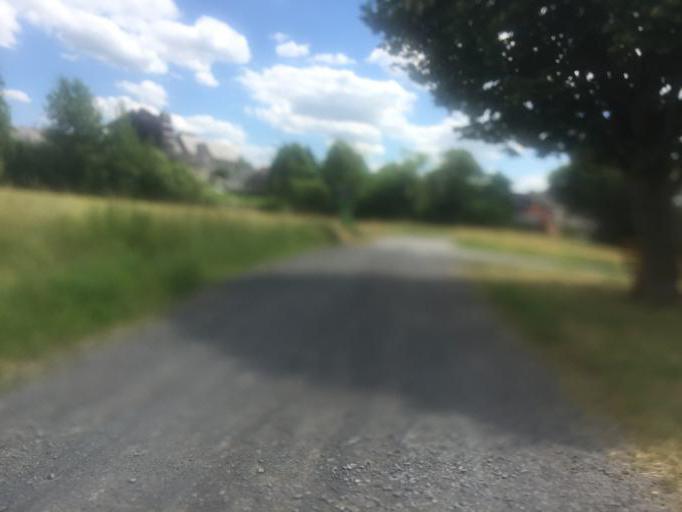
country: DE
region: Rheinland-Pfalz
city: Steinefrenz
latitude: 50.4618
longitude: 7.9315
